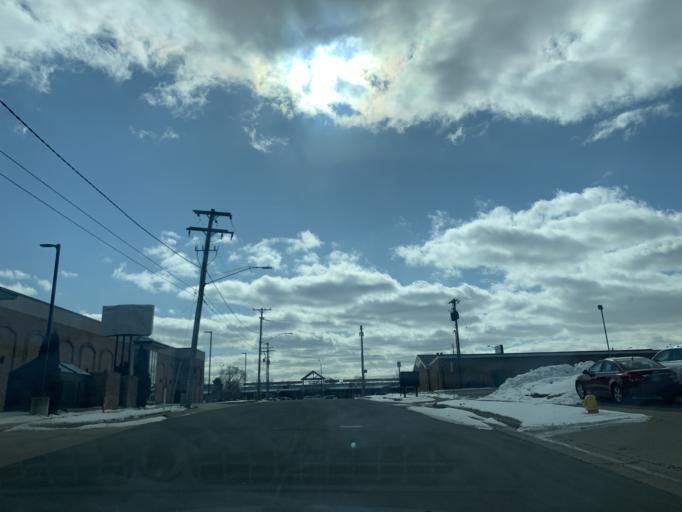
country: US
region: Michigan
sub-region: Kent County
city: Wyoming
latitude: 42.9146
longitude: -85.6913
